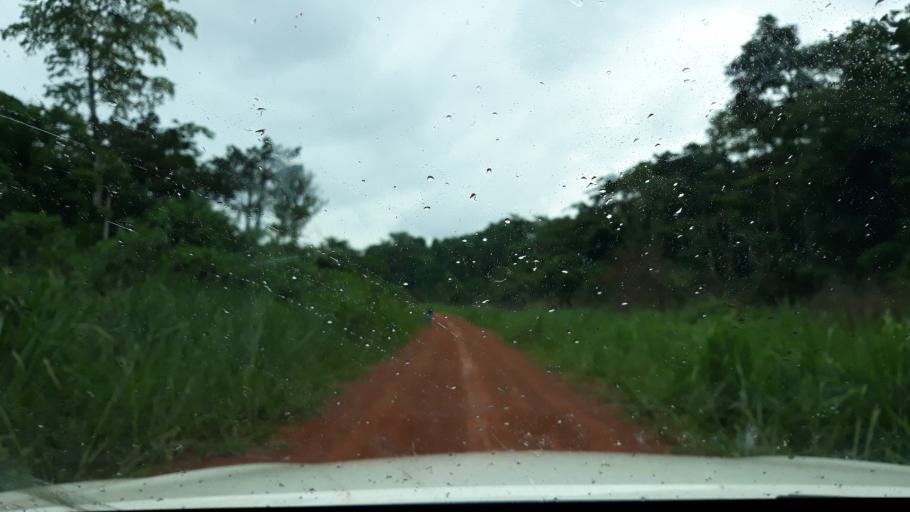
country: CD
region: Equateur
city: Libenge
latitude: 3.6979
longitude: 18.7398
